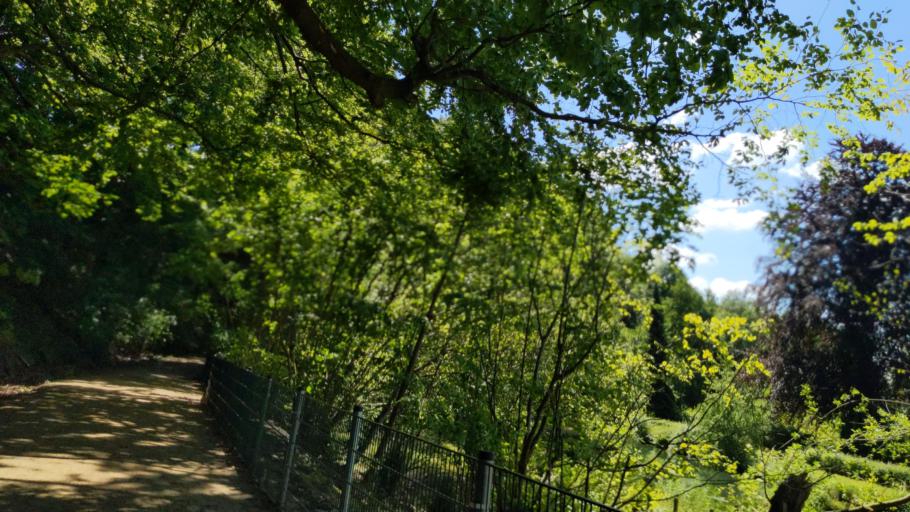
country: DE
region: Schleswig-Holstein
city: Ratzeburg
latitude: 53.6904
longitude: 10.7781
